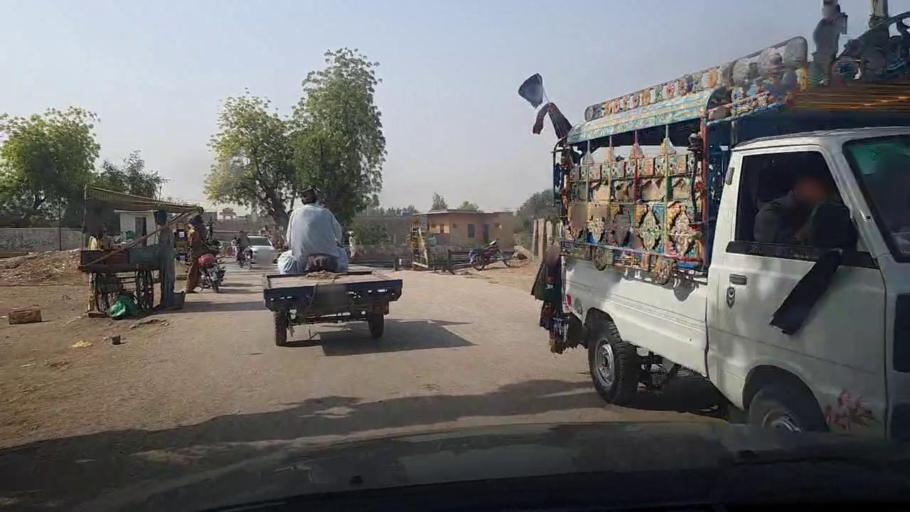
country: PK
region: Sindh
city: Mirpur Mathelo
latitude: 28.0192
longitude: 69.5508
